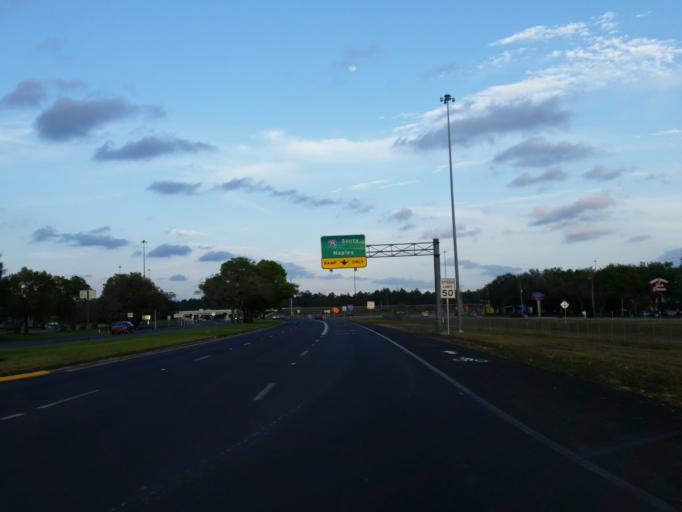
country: US
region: Florida
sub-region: Hillsborough County
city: Temple Terrace
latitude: 28.0691
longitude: -82.3593
